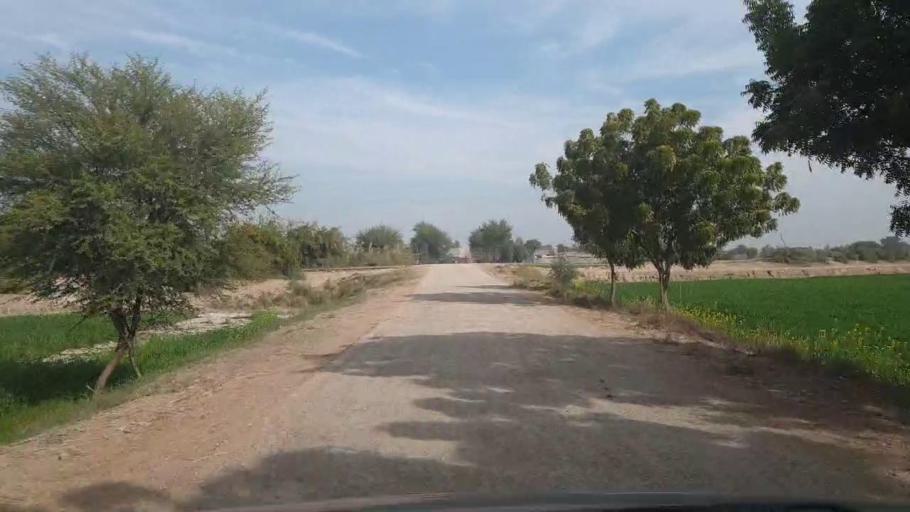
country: PK
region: Sindh
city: Khadro
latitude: 26.1565
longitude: 68.6955
